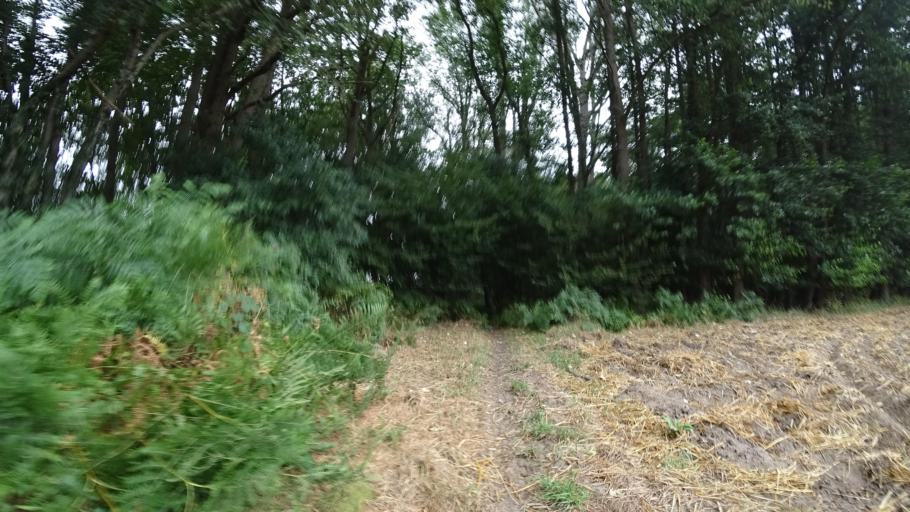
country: DE
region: North Rhine-Westphalia
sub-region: Regierungsbezirk Detmold
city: Guetersloh
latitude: 51.9136
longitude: 8.3188
